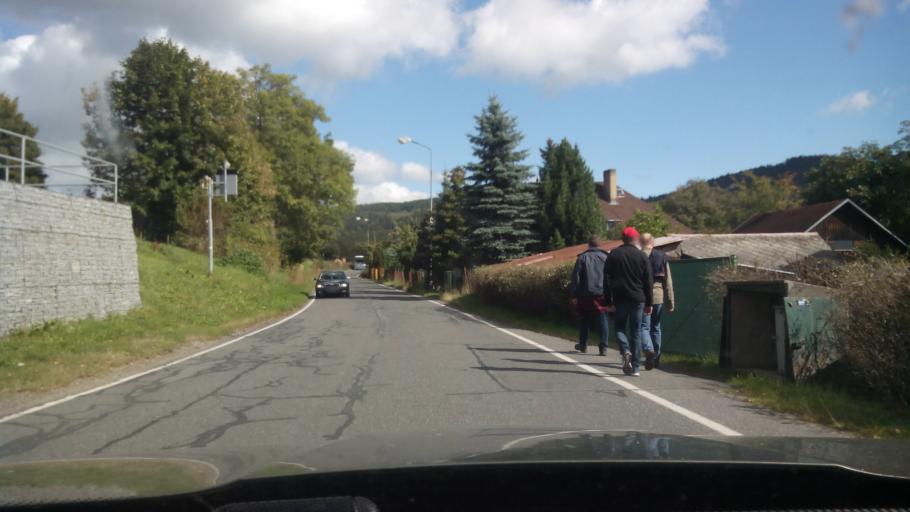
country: CZ
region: Plzensky
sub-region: Okres Klatovy
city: Kasperske Hory
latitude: 49.1453
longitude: 13.5616
